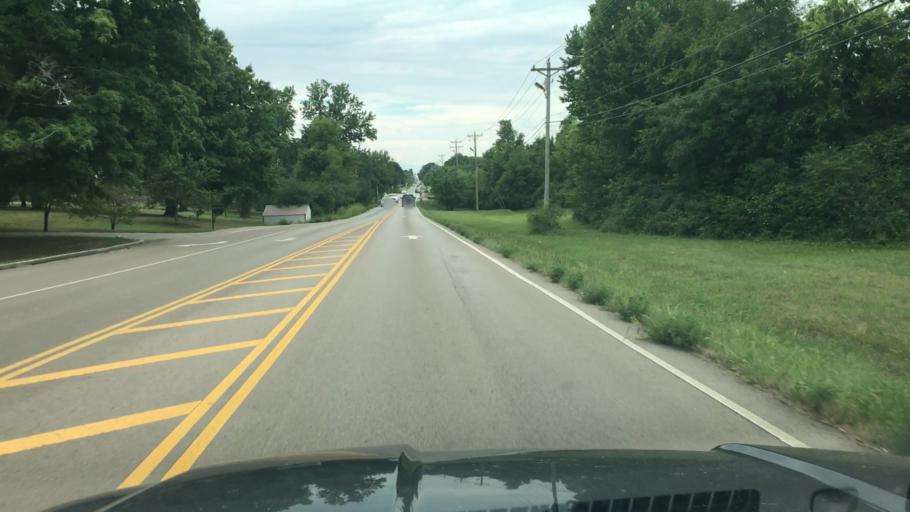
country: US
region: Tennessee
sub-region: Williamson County
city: Thompson's Station
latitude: 35.7733
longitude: -86.8803
